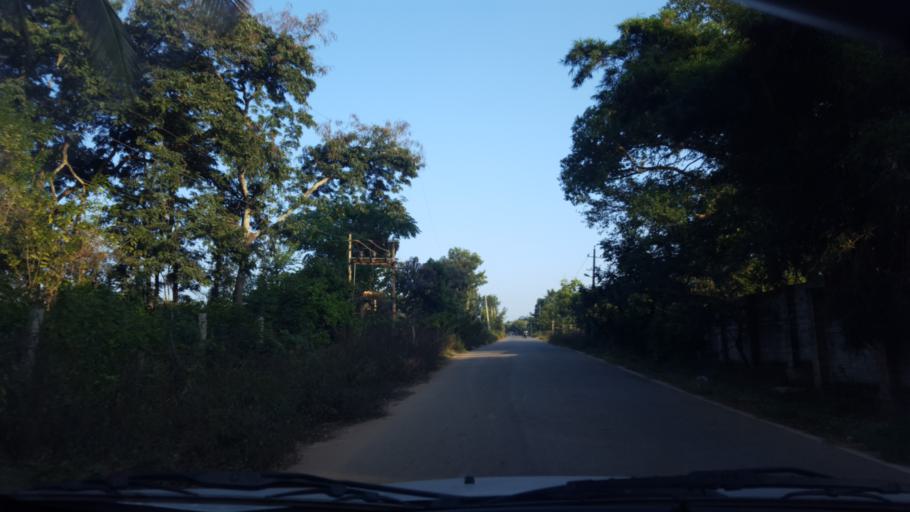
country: IN
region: Karnataka
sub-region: Bangalore Urban
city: Yelahanka
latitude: 13.1735
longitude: 77.5960
